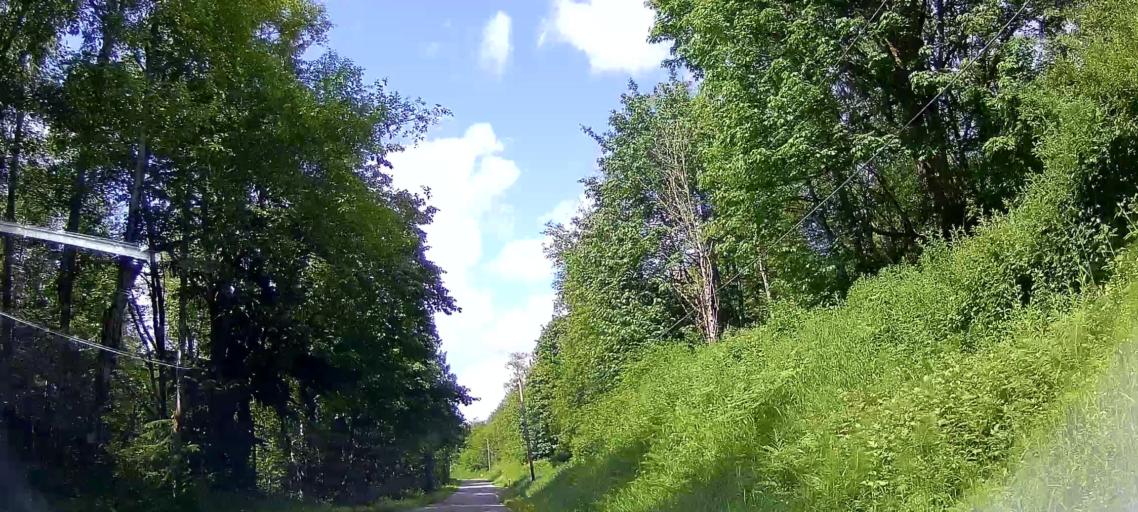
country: US
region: Washington
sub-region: Whatcom County
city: Sudden Valley
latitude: 48.6680
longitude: -122.1951
